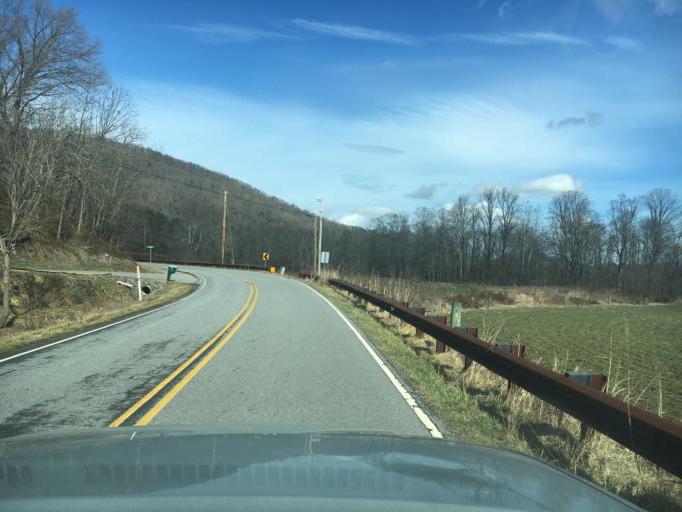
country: US
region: North Carolina
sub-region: Haywood County
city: Clyde
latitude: 35.4916
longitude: -82.8844
